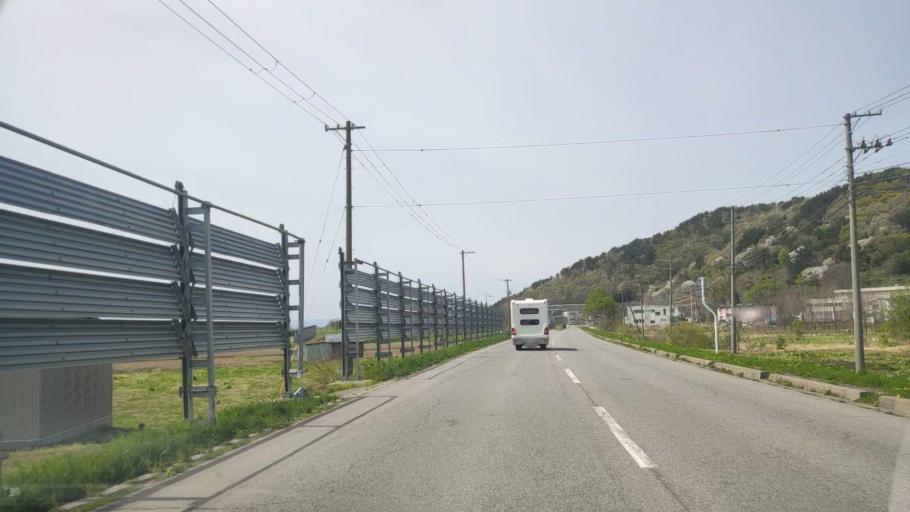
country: JP
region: Aomori
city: Aomori Shi
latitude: 40.8274
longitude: 140.8536
